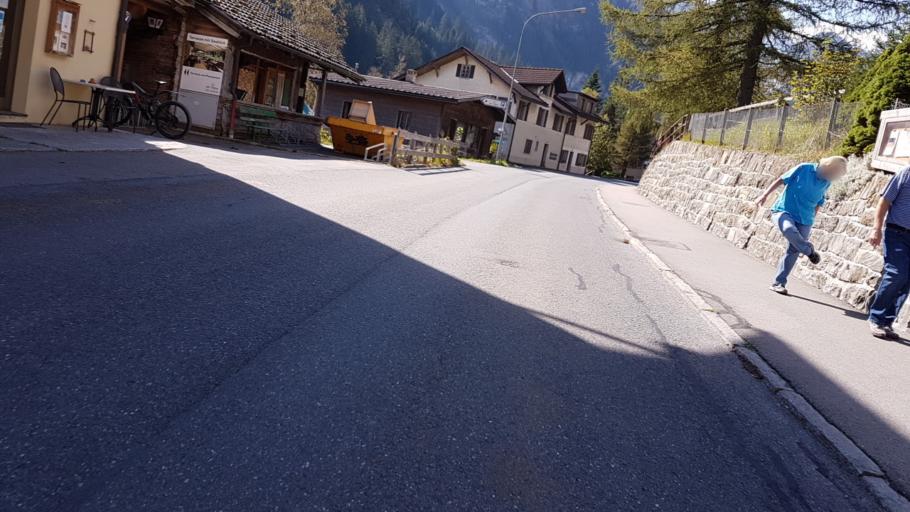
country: CH
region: Bern
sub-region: Frutigen-Niedersimmental District
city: Kandersteg
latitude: 46.4900
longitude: 7.6713
